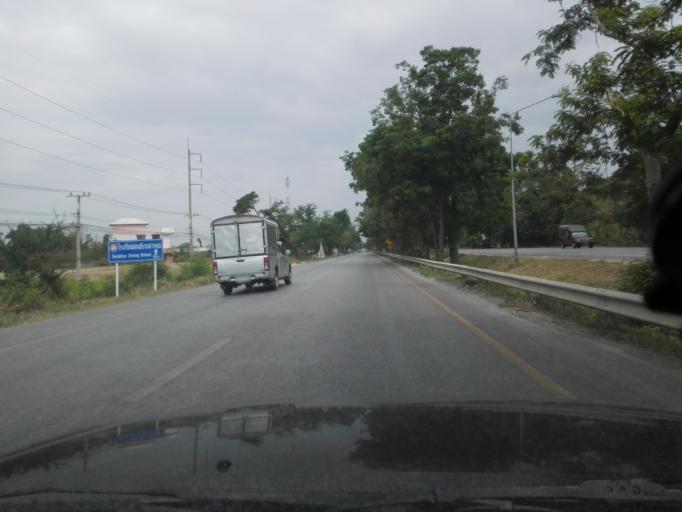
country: TH
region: Nakhon Sawan
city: Nakhon Sawan
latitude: 15.7289
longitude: 100.0373
